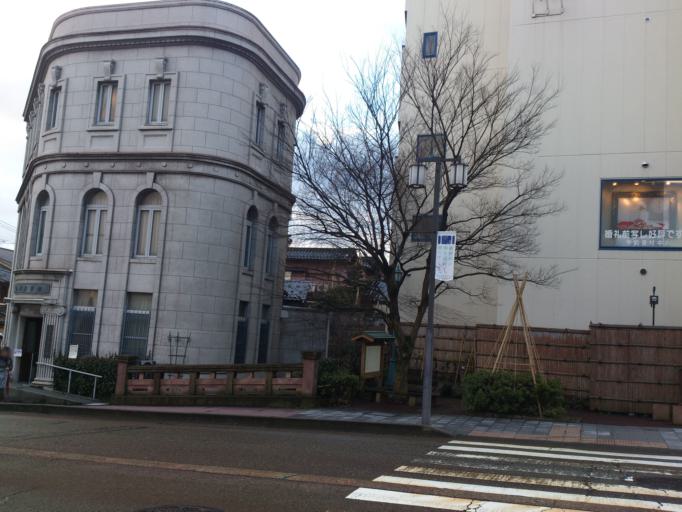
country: JP
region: Ishikawa
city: Kanazawa-shi
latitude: 36.5711
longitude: 136.6636
